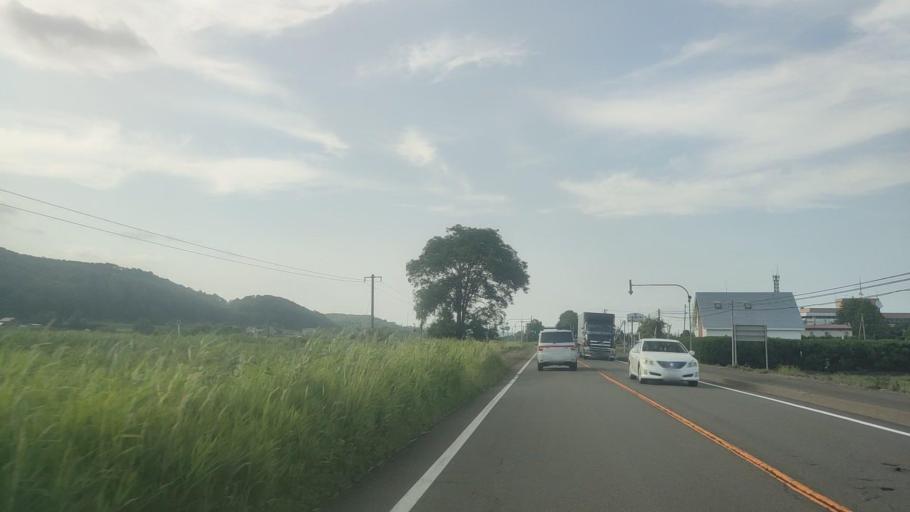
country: JP
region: Hokkaido
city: Iwamizawa
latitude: 42.9970
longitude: 141.7897
